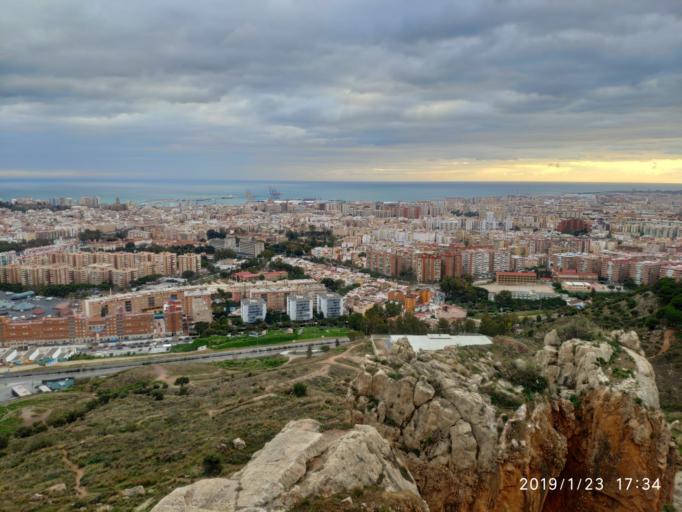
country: ES
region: Andalusia
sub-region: Provincia de Malaga
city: Malaga
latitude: 36.7383
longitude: -4.4381
